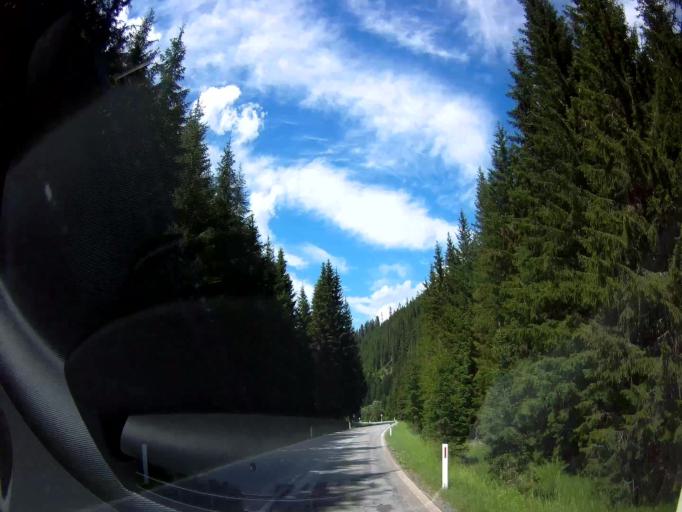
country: AT
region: Styria
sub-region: Politischer Bezirk Murau
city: Stadl an der Mur
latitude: 47.0087
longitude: 14.0093
